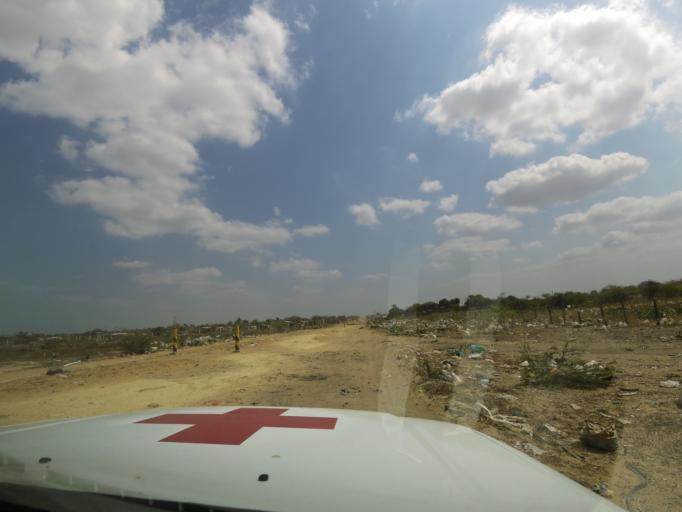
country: CO
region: La Guajira
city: Riohacha
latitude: 11.5216
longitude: -72.9201
